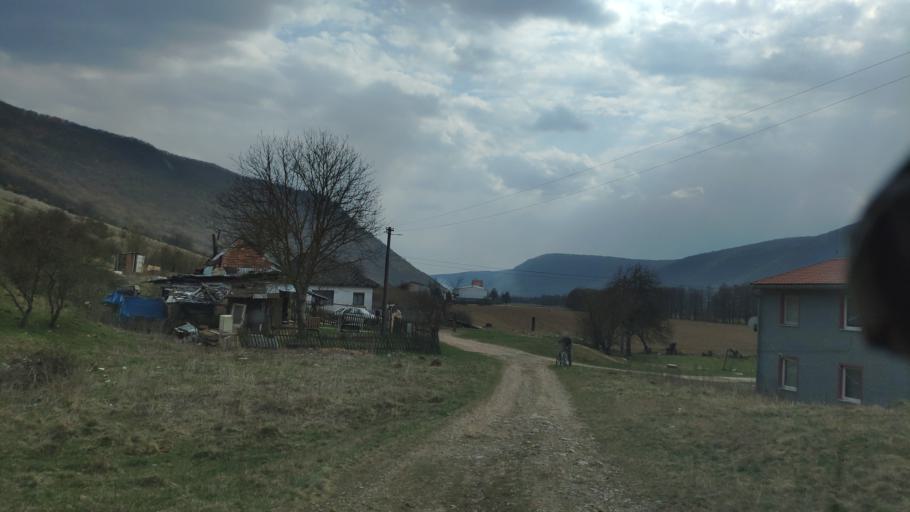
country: SK
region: Kosicky
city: Roznava
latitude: 48.6137
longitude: 20.3883
